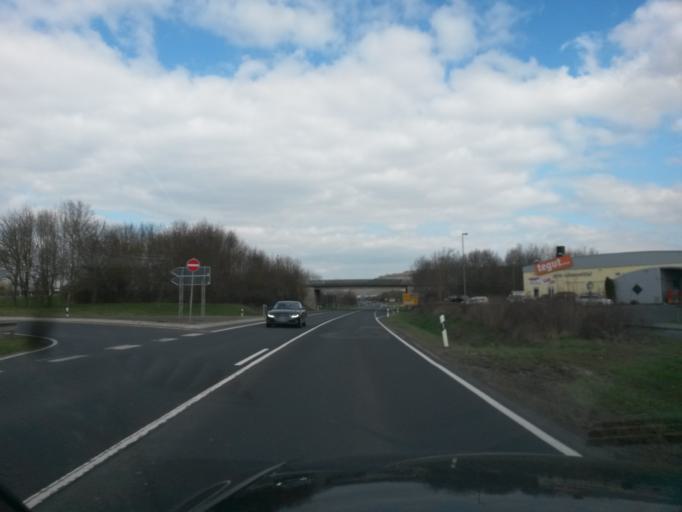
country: DE
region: Bavaria
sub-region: Regierungsbezirk Unterfranken
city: Eibelstadt
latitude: 49.7292
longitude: 9.9927
